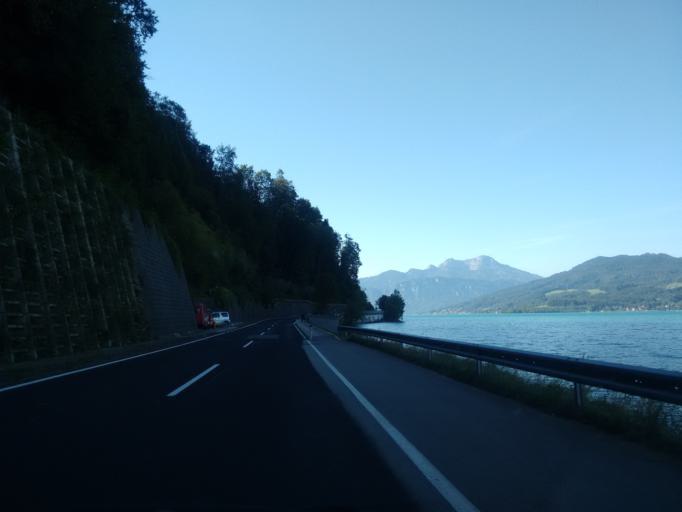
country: AT
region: Upper Austria
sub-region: Politischer Bezirk Vocklabruck
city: Steinbach am Attersee
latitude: 47.8531
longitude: 13.5565
